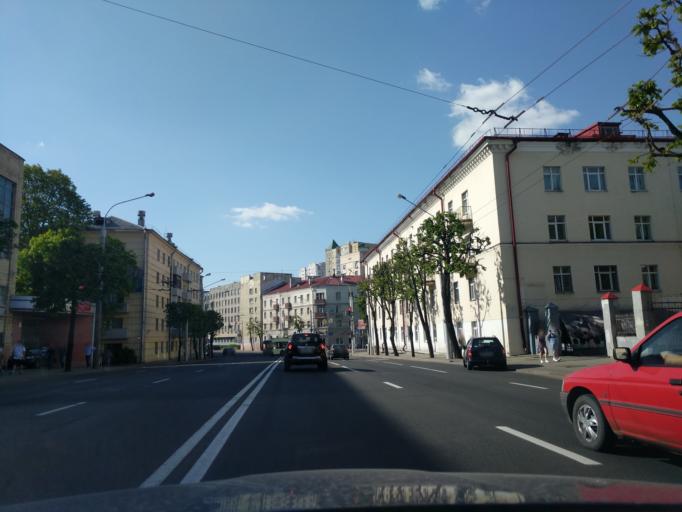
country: BY
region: Minsk
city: Minsk
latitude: 53.9238
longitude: 27.5996
